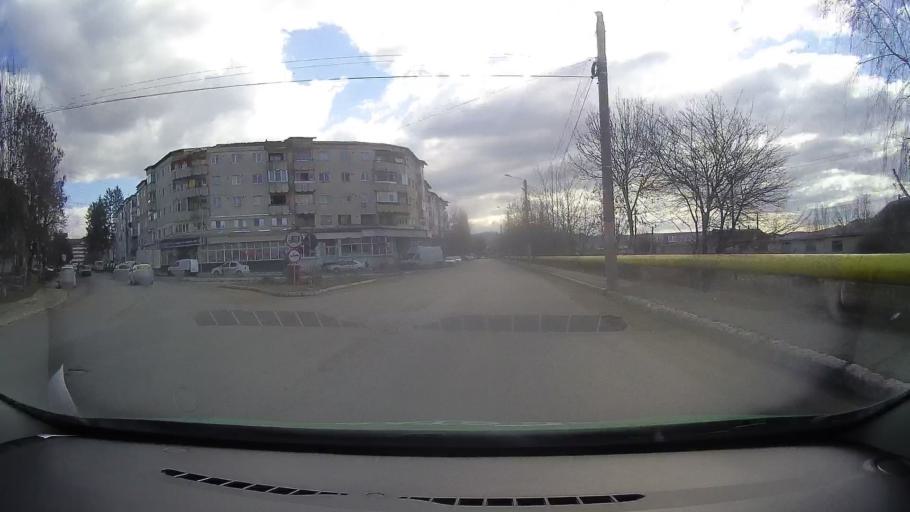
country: RO
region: Dambovita
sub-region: Oras Pucioasa
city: Pucioasa
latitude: 45.0784
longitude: 25.4292
